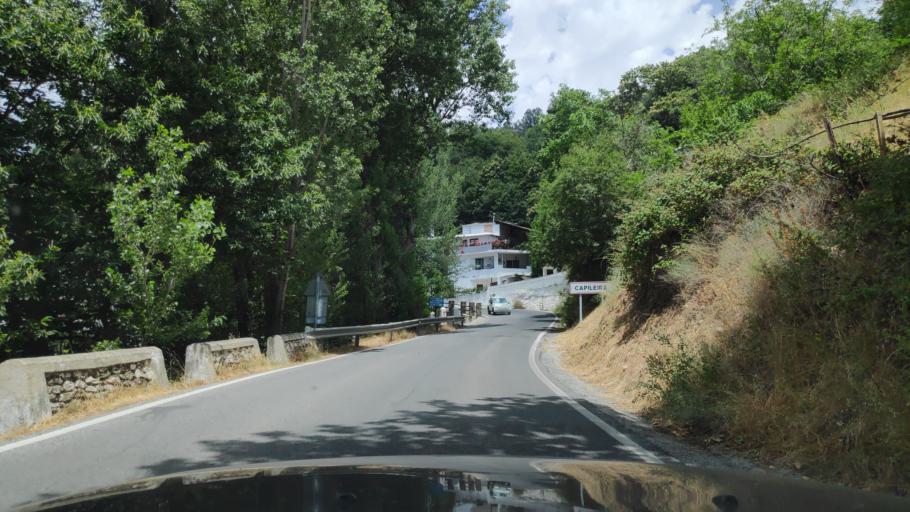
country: ES
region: Andalusia
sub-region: Provincia de Granada
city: Capileira
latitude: 36.9592
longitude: -3.3570
